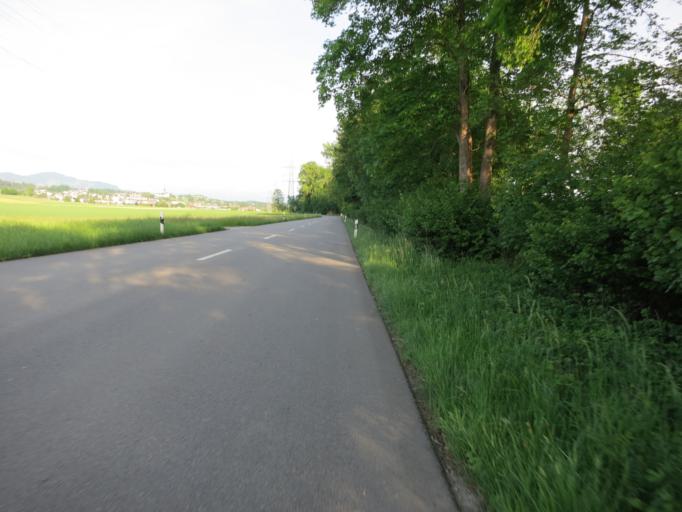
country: CH
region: Zurich
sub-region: Bezirk Uster
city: Moenchaltorf / Dorf
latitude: 47.3080
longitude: 8.7316
